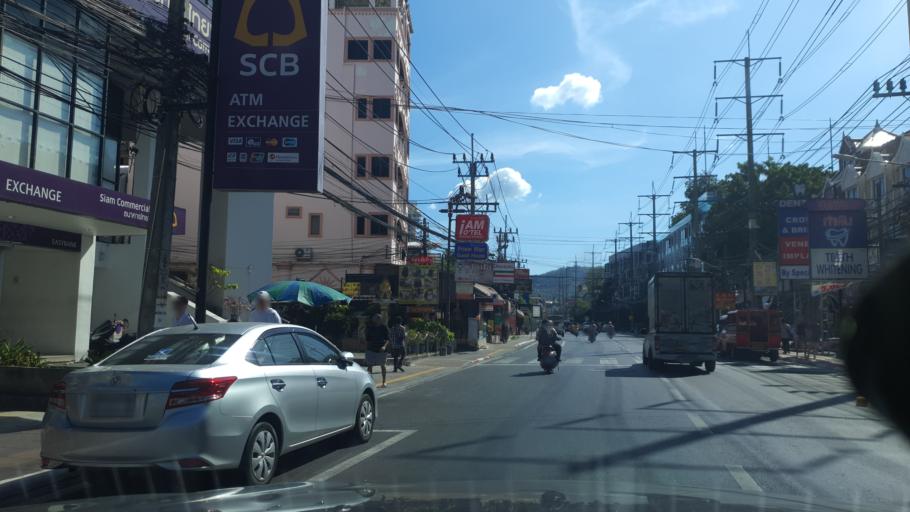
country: TH
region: Phuket
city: Patong
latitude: 7.9000
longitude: 98.3004
